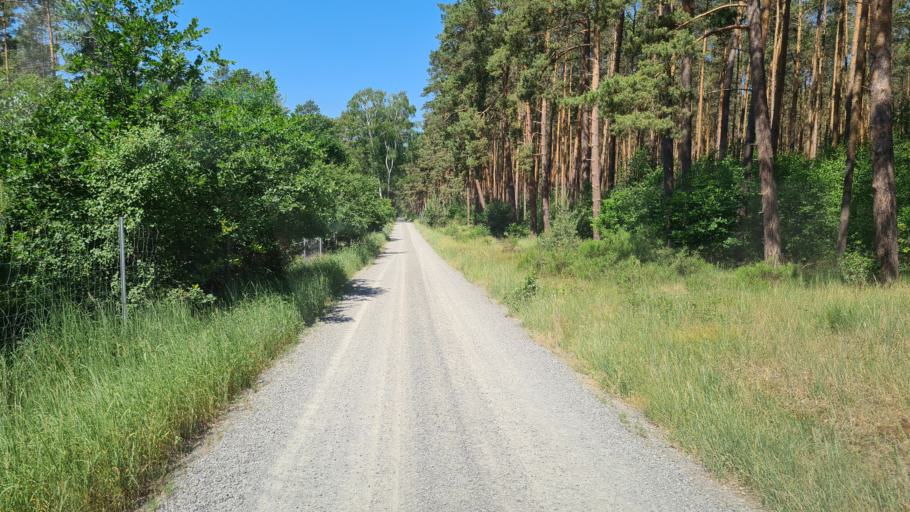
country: DE
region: Brandenburg
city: Lebusa
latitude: 51.7754
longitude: 13.4011
